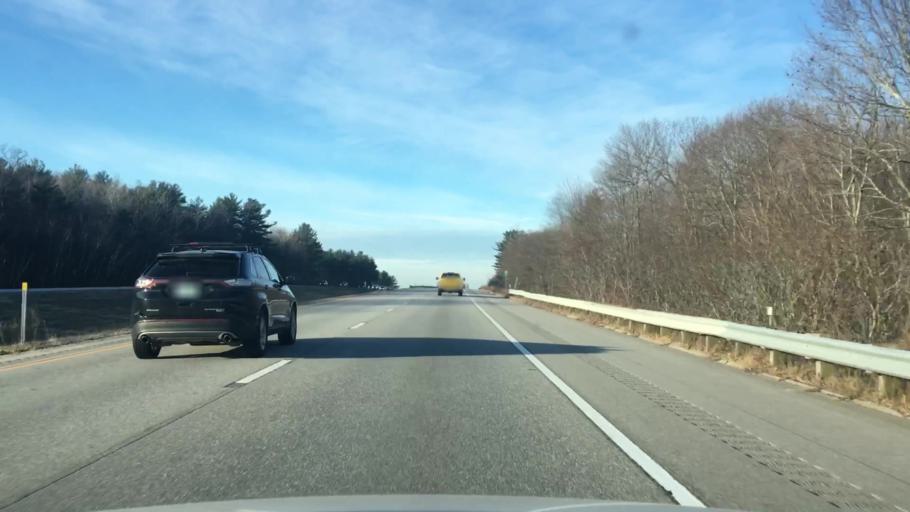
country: US
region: New Hampshire
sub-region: Rockingham County
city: Candia
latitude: 43.0409
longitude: -71.2887
